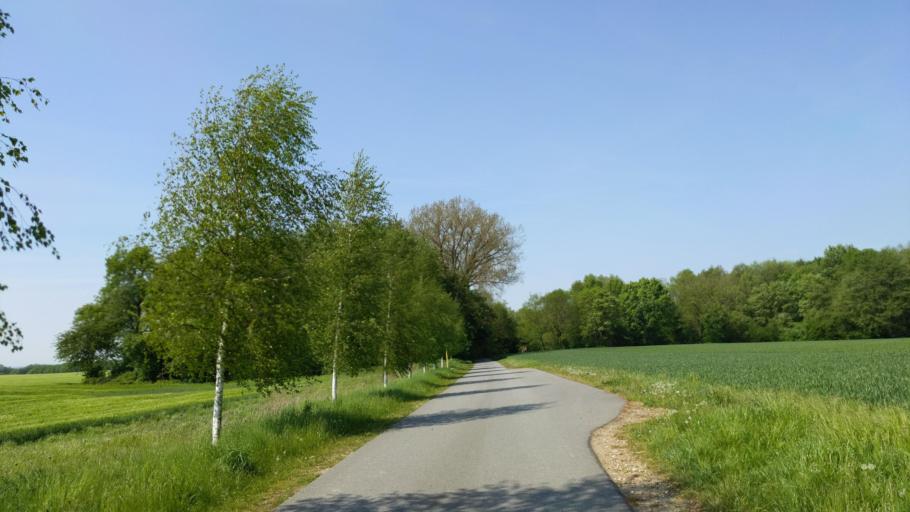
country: DE
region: Mecklenburg-Vorpommern
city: Selmsdorf
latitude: 53.8790
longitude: 10.8949
